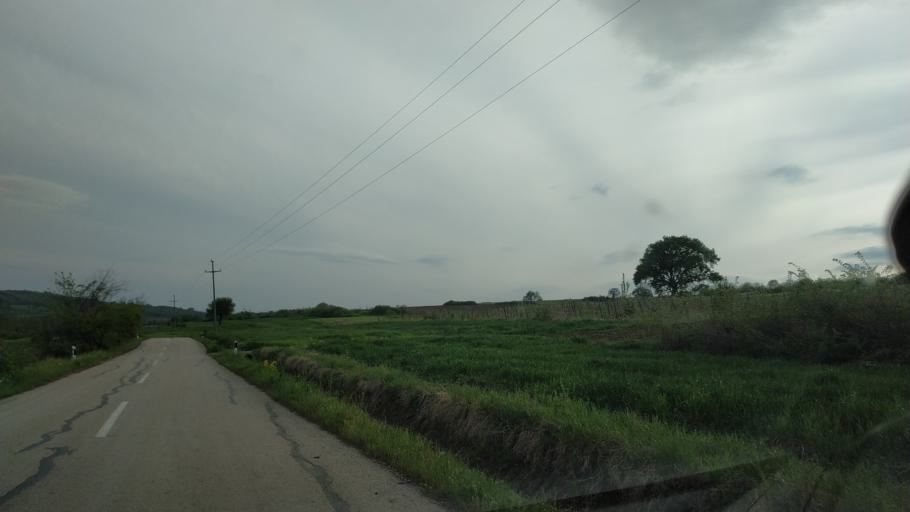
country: RS
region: Central Serbia
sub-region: Zajecarski Okrug
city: Soko Banja
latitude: 43.5166
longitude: 21.8458
